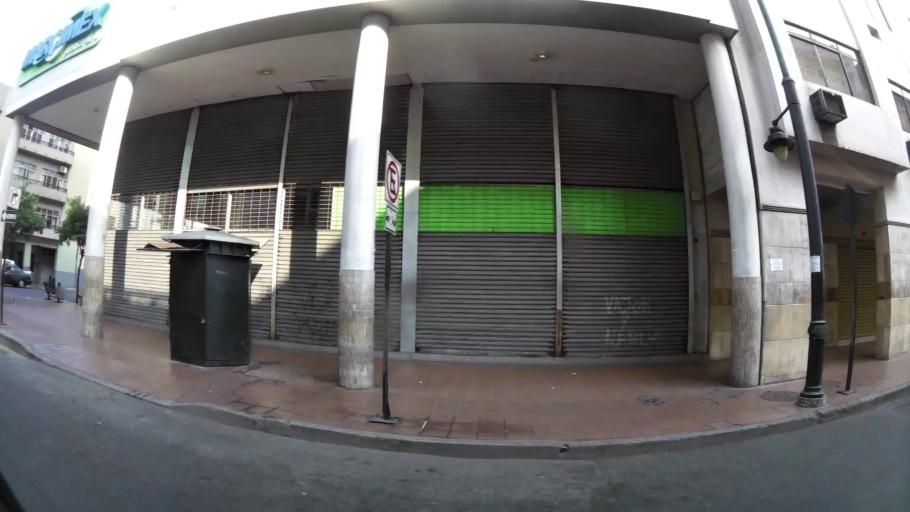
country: EC
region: Guayas
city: Guayaquil
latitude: -2.1904
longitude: -79.8853
